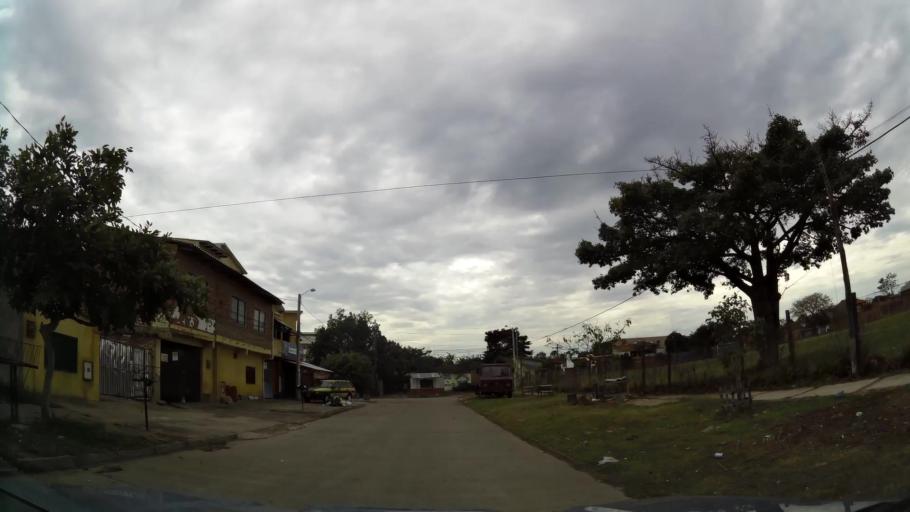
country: BO
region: Santa Cruz
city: Santa Cruz de la Sierra
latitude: -17.7525
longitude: -63.1794
